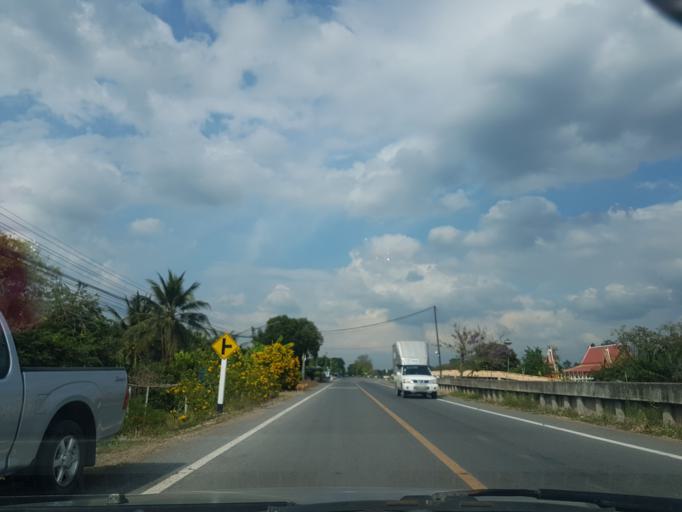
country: TH
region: Pathum Thani
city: Nong Suea
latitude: 14.1762
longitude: 100.8915
